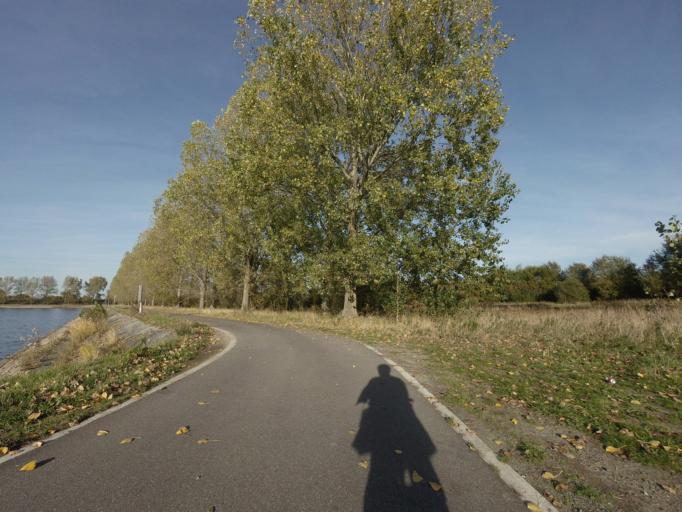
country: NL
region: North Brabant
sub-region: Gemeente Woensdrecht
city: Woensdrecht
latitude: 51.3711
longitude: 4.3035
